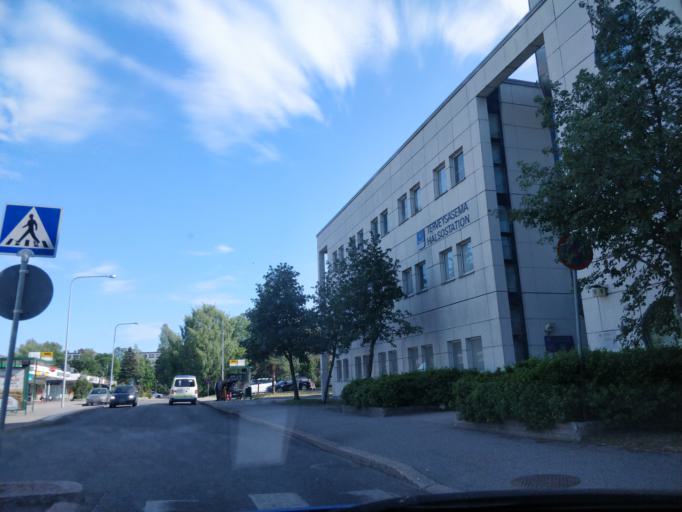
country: FI
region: Uusimaa
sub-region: Helsinki
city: Vantaa
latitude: 60.2346
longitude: 25.0099
